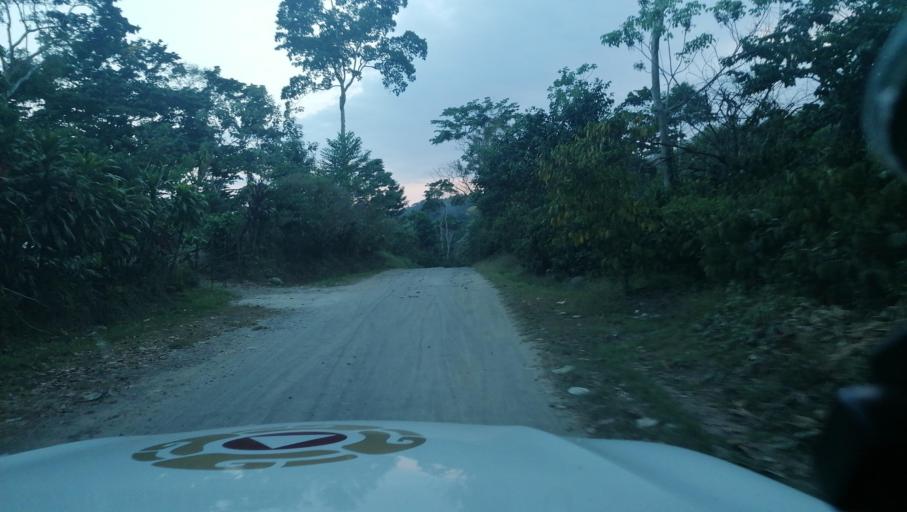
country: MX
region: Chiapas
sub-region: Cacahoatan
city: Benito Juarez
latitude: 15.0571
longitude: -92.2422
